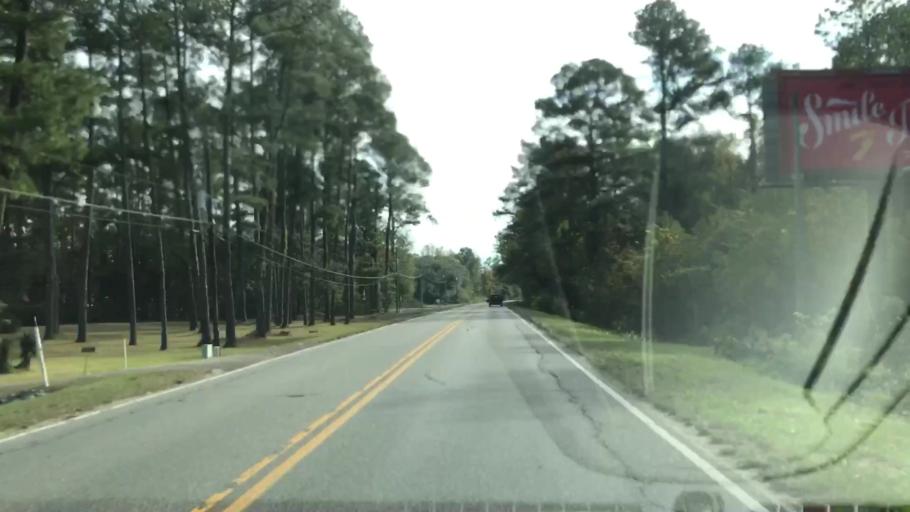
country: US
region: South Carolina
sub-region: Colleton County
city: Walterboro
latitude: 32.8944
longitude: -80.6352
